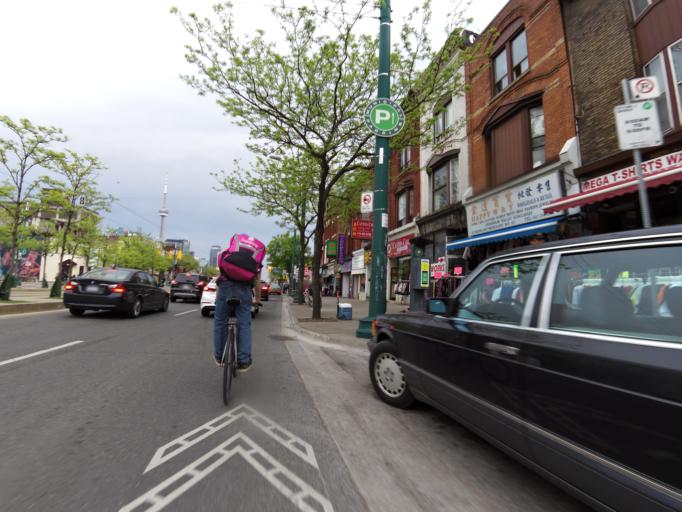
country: CA
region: Ontario
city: Toronto
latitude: 43.6566
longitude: -79.3996
